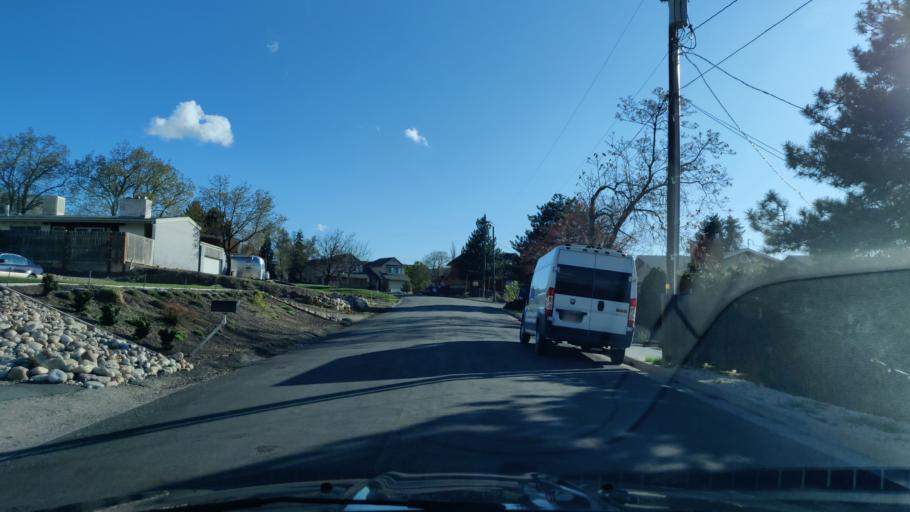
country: US
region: Utah
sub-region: Salt Lake County
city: Little Cottonwood Creek Valley
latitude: 40.6159
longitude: -111.8267
